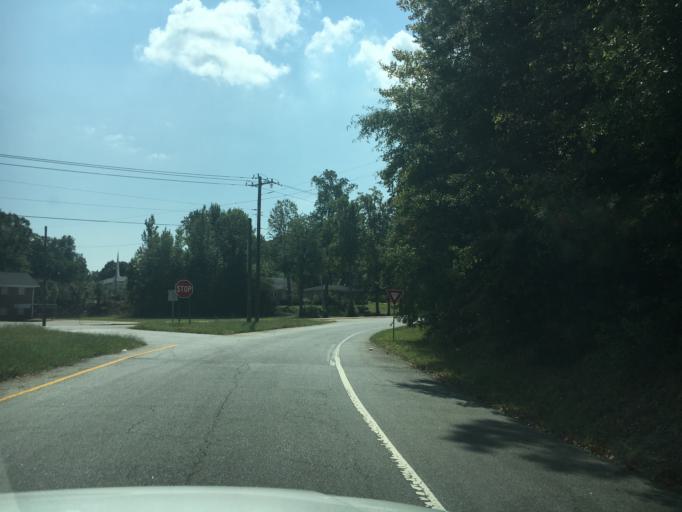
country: US
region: South Carolina
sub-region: Greenville County
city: Gantt
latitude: 34.8072
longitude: -82.4226
